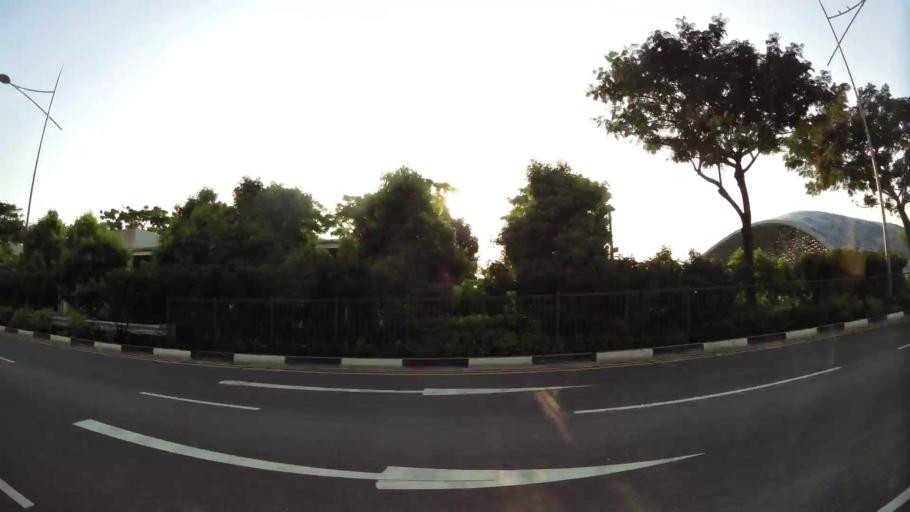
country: SG
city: Singapore
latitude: 1.2818
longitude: 103.8608
